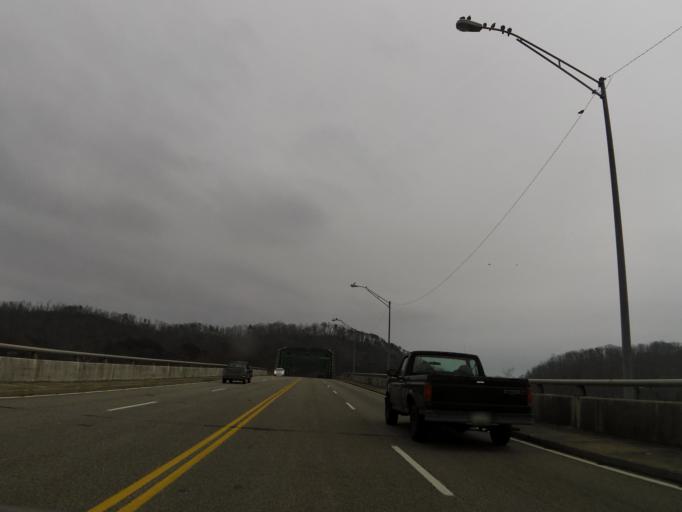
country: US
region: Tennessee
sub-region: Anderson County
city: Clinton
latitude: 36.0951
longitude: -84.1339
